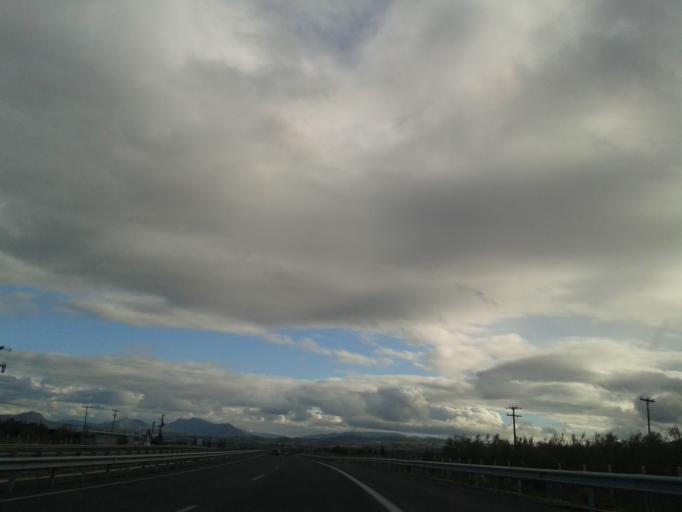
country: GR
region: Peloponnese
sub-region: Nomos Korinthias
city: Velo
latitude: 37.9586
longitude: 22.7497
